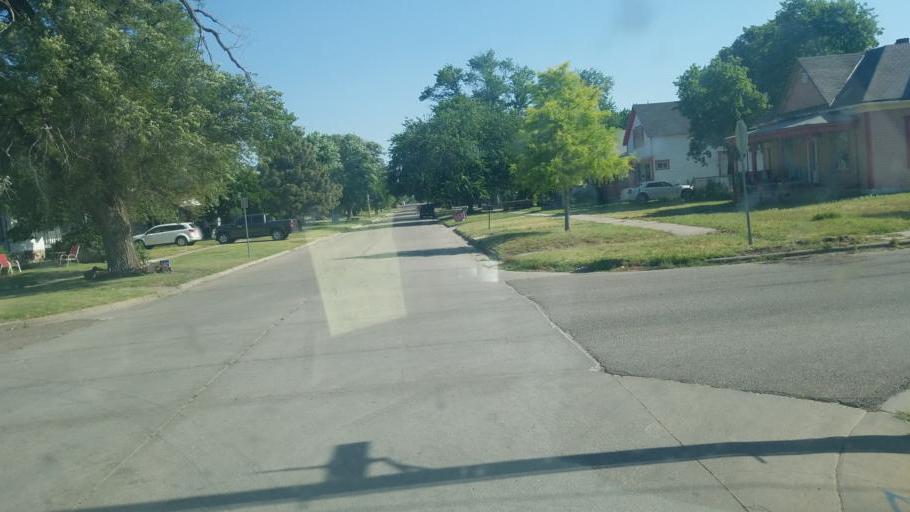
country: US
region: Kansas
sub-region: Barton County
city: Great Bend
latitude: 38.3621
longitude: -98.7692
